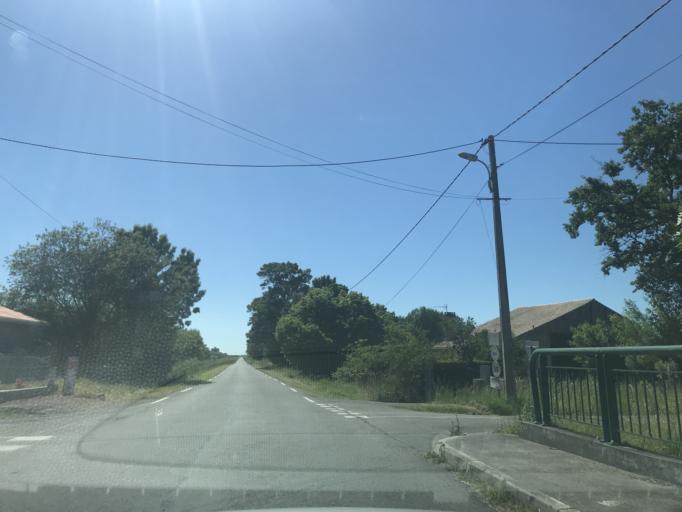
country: FR
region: Aquitaine
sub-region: Departement de la Gironde
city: Saint-Ciers-sur-Gironde
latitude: 45.2914
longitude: -0.6304
